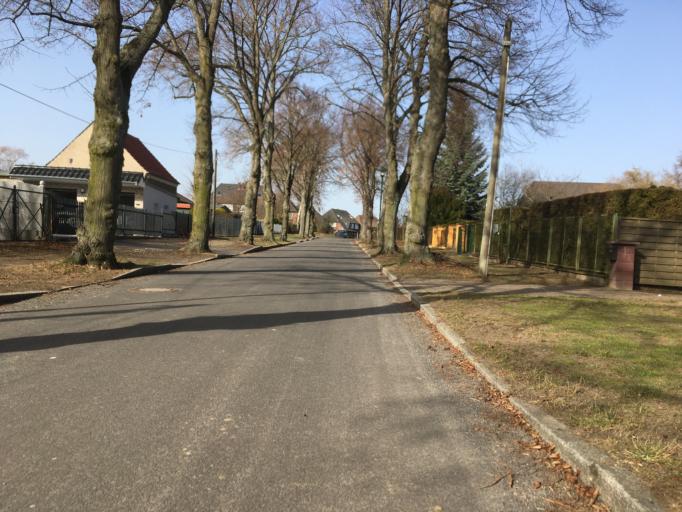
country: DE
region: Berlin
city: Buch
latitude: 52.6752
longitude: 13.5225
